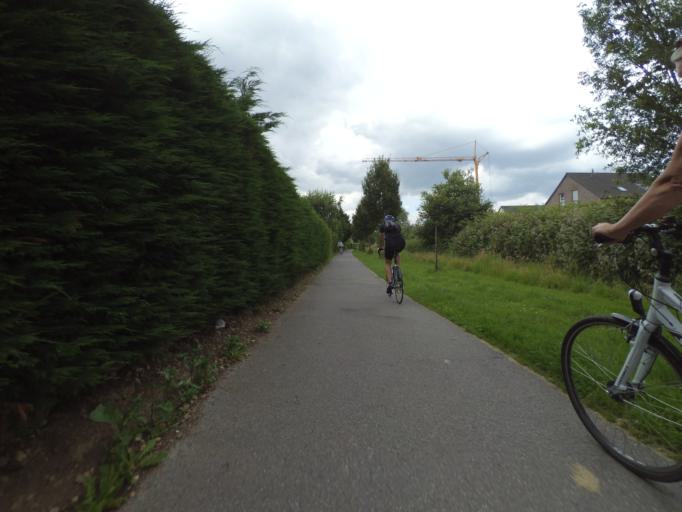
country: DE
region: North Rhine-Westphalia
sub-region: Regierungsbezirk Koln
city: Wurselen
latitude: 50.7457
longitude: 6.1520
